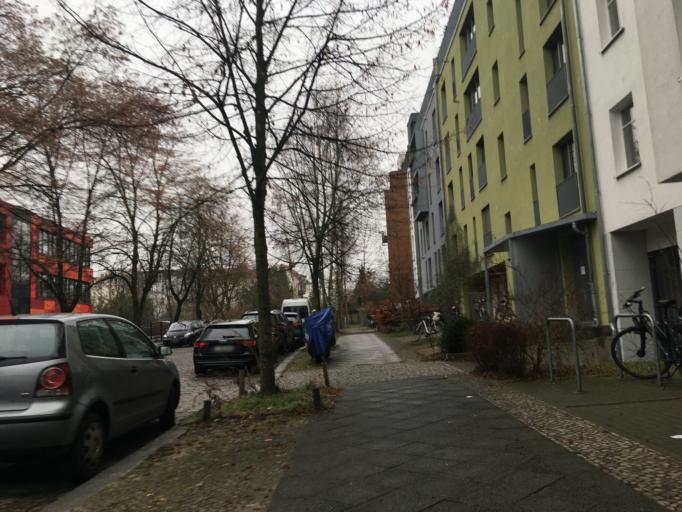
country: DE
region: Berlin
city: Pankow
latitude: 52.5653
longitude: 13.4184
